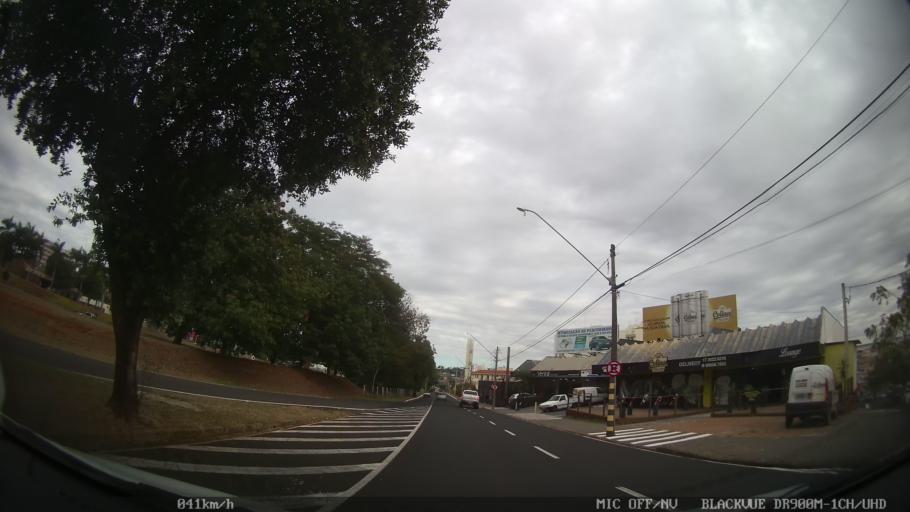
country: BR
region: Sao Paulo
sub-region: Sao Jose Do Rio Preto
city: Sao Jose do Rio Preto
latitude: -20.8233
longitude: -49.3979
